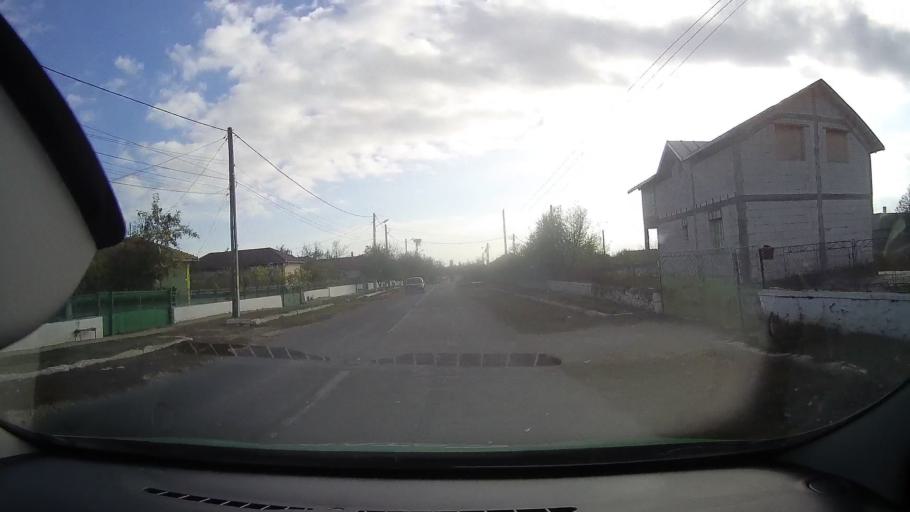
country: RO
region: Constanta
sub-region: Comuna Corbu
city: Corbu
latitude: 44.4212
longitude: 28.6605
